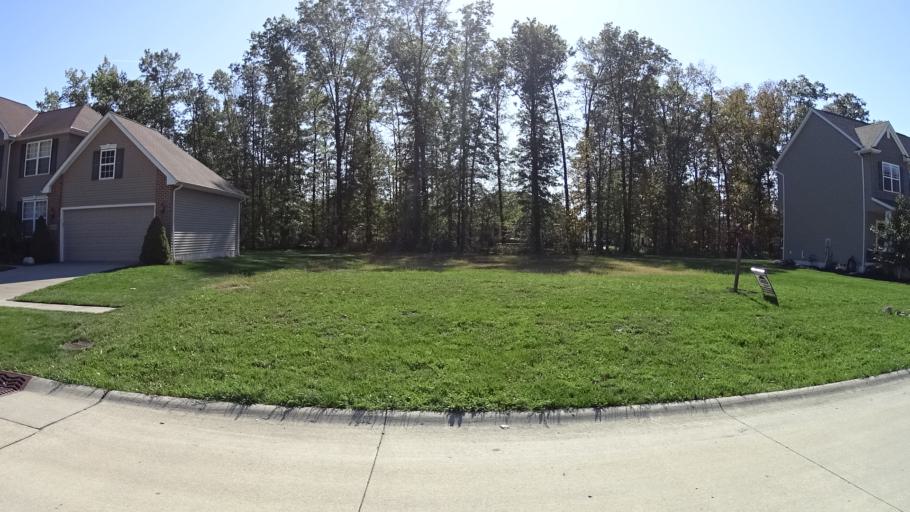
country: US
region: Ohio
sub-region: Lorain County
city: Vermilion-on-the-Lake
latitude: 41.4169
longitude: -82.3383
